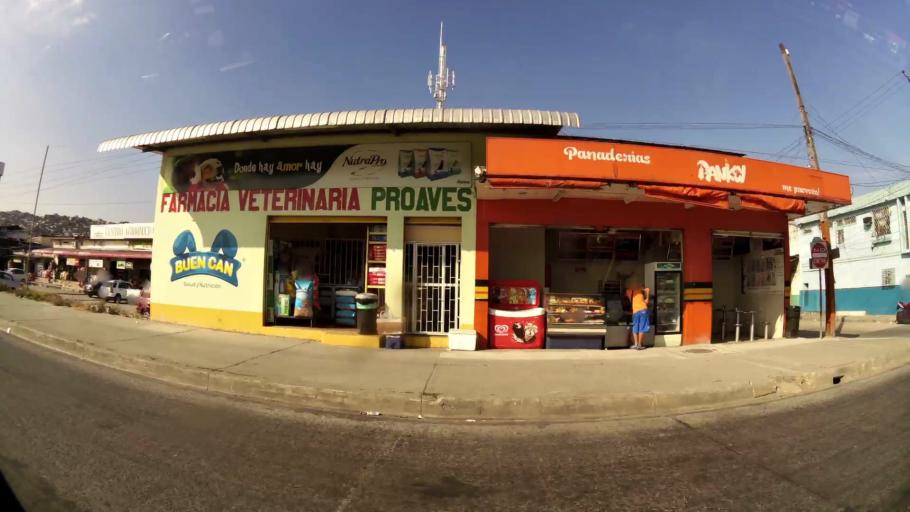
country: EC
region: Guayas
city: Guayaquil
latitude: -2.1573
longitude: -79.9292
